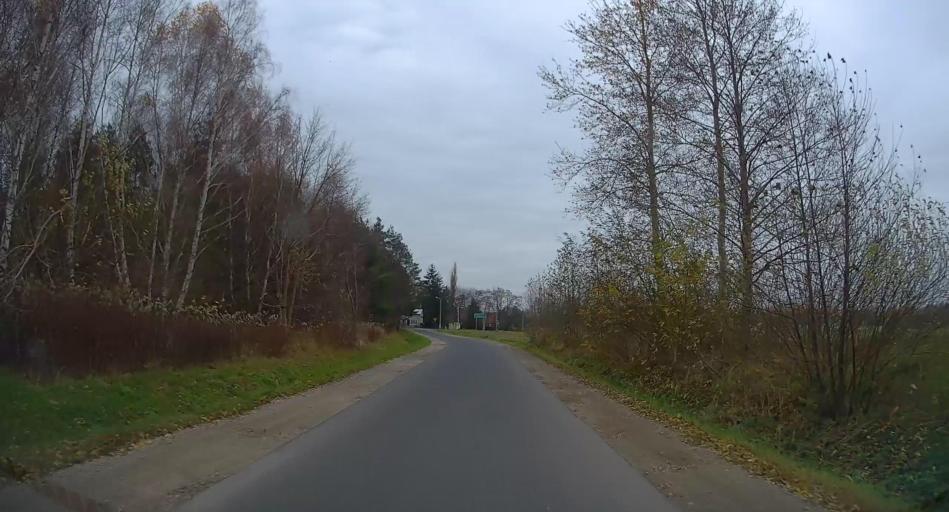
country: PL
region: Lodz Voivodeship
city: Zabia Wola
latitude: 51.9905
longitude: 20.6605
